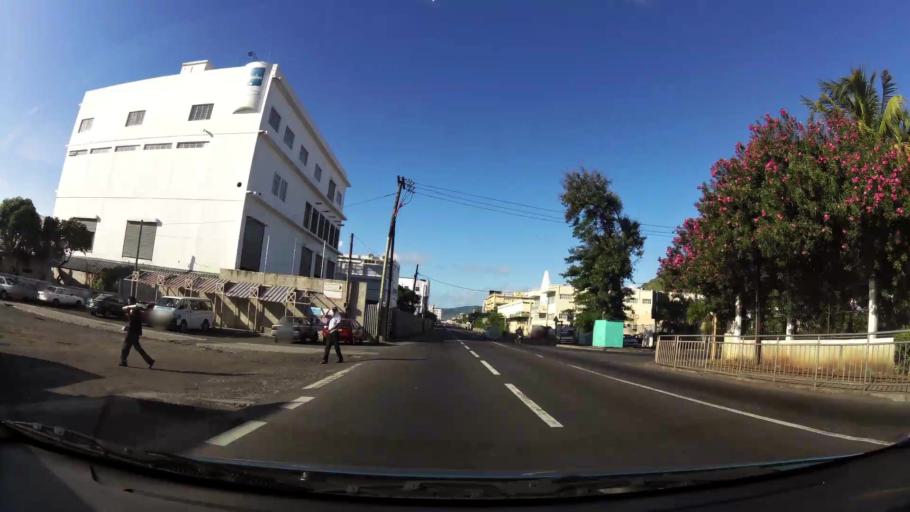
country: MU
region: Port Louis
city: Port Louis
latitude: -20.1695
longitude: 57.4821
